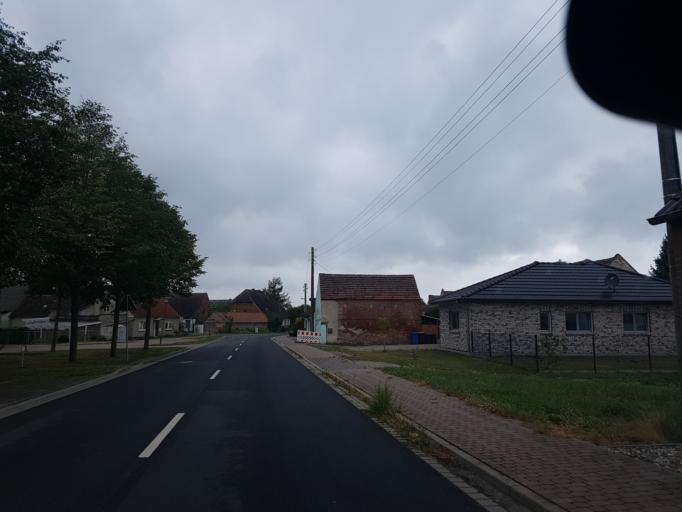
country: DE
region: Saxony-Anhalt
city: Tucheim
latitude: 52.3133
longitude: 12.1215
